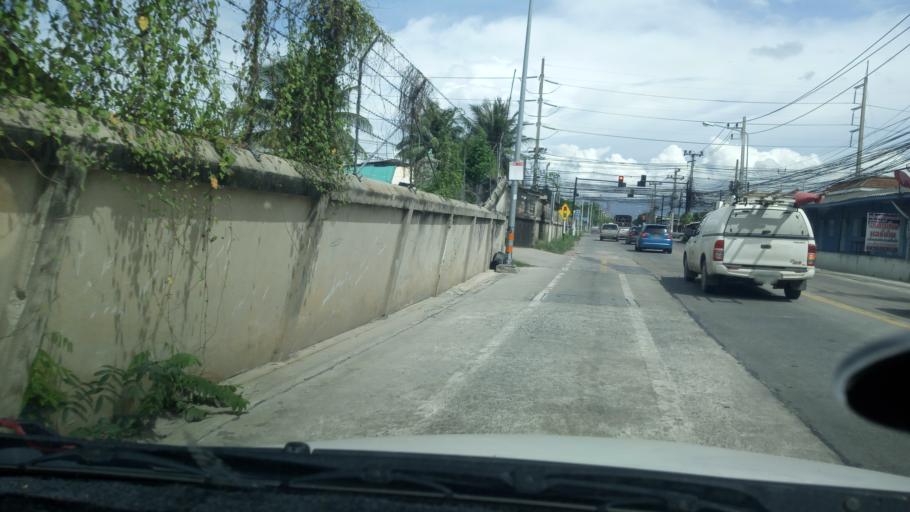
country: TH
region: Chon Buri
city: Chon Buri
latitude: 13.4017
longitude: 101.0302
